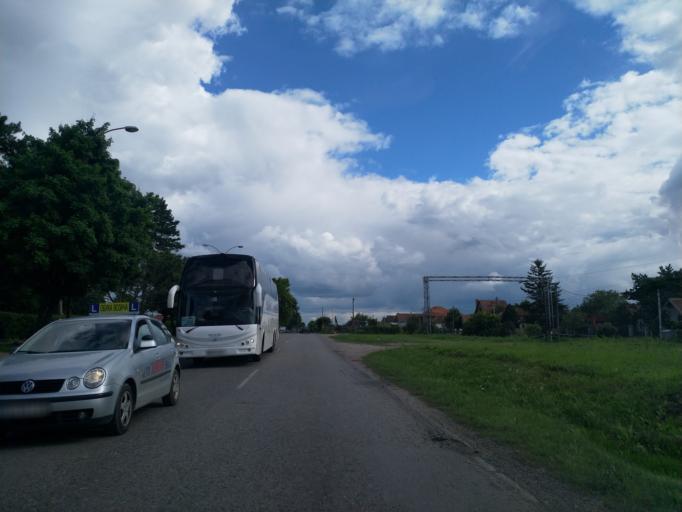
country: RS
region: Central Serbia
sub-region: Pomoravski Okrug
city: Cuprija
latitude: 43.9137
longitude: 21.3762
